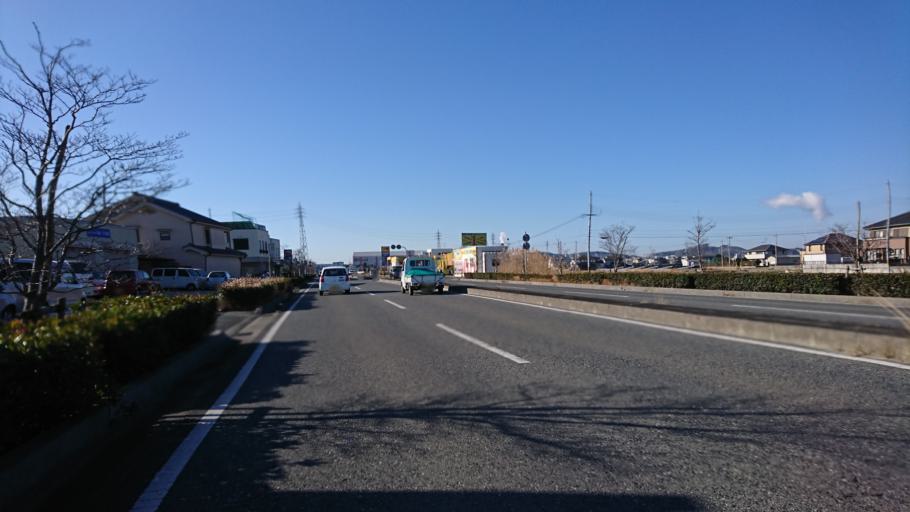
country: JP
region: Hyogo
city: Kakogawacho-honmachi
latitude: 34.7928
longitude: 134.8242
